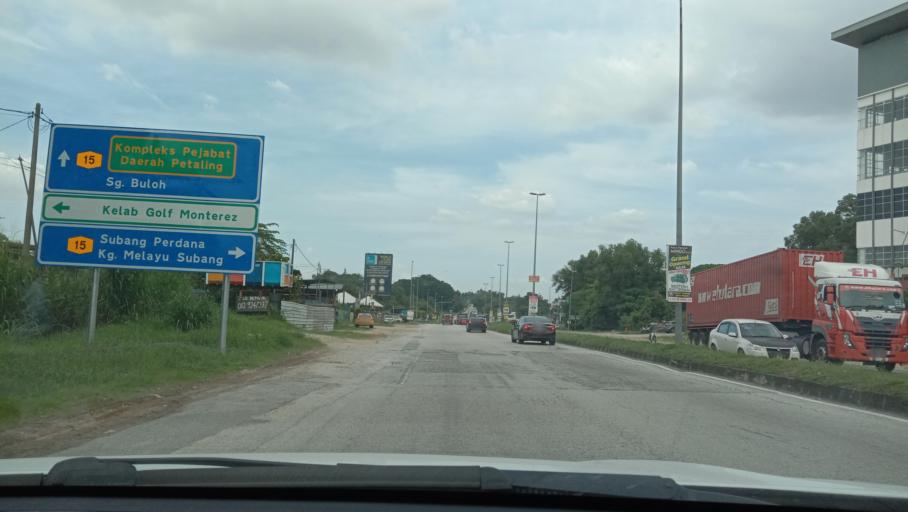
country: MY
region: Selangor
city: Kampung Baru Subang
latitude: 3.1357
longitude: 101.5258
